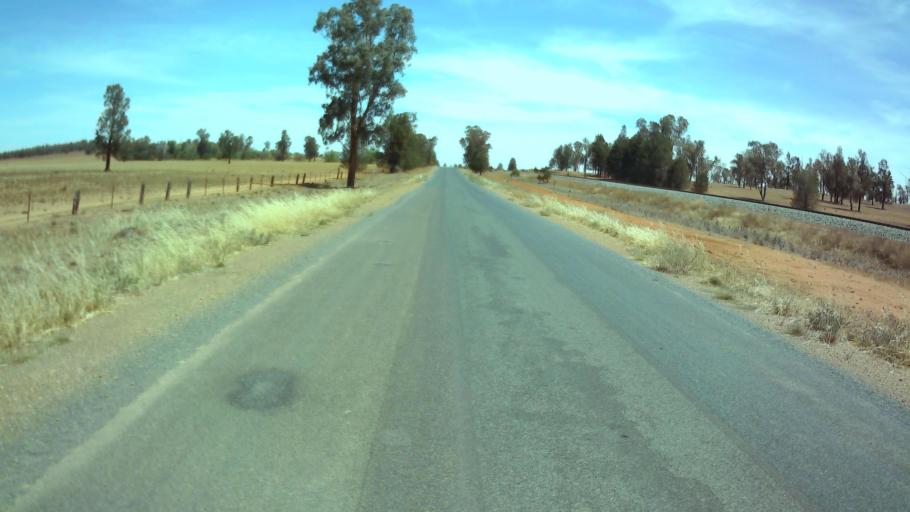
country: AU
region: New South Wales
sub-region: Weddin
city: Grenfell
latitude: -33.7693
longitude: 147.7576
